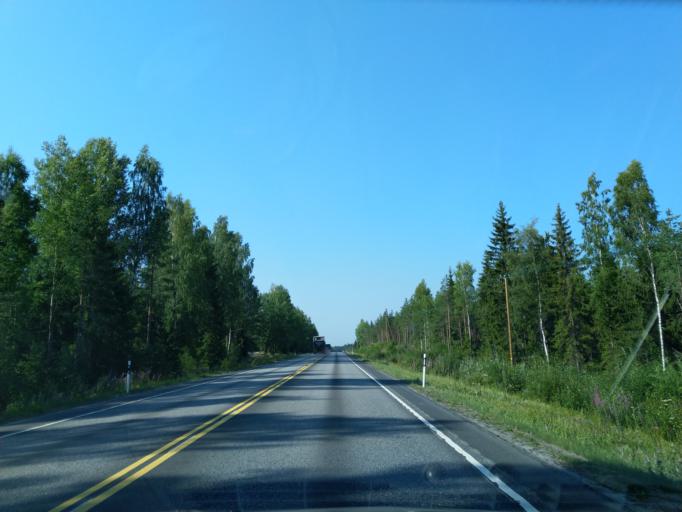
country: FI
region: Satakunta
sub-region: Pori
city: Pomarkku
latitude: 61.7224
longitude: 22.0567
